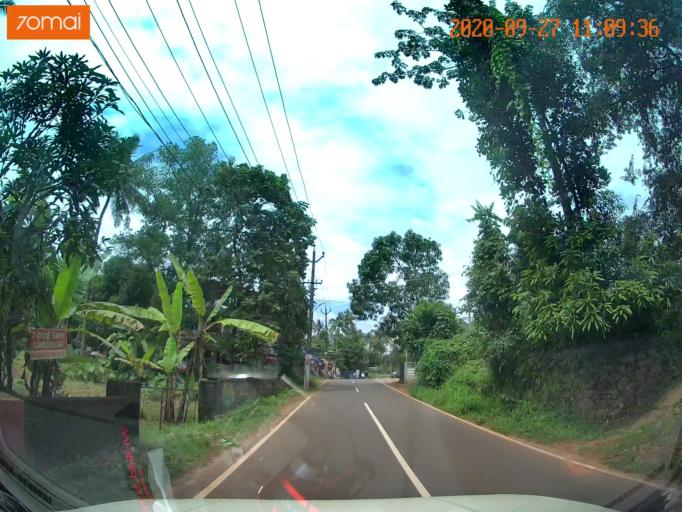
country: IN
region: Kerala
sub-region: Thrissur District
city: Trichur
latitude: 10.4301
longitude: 76.2269
